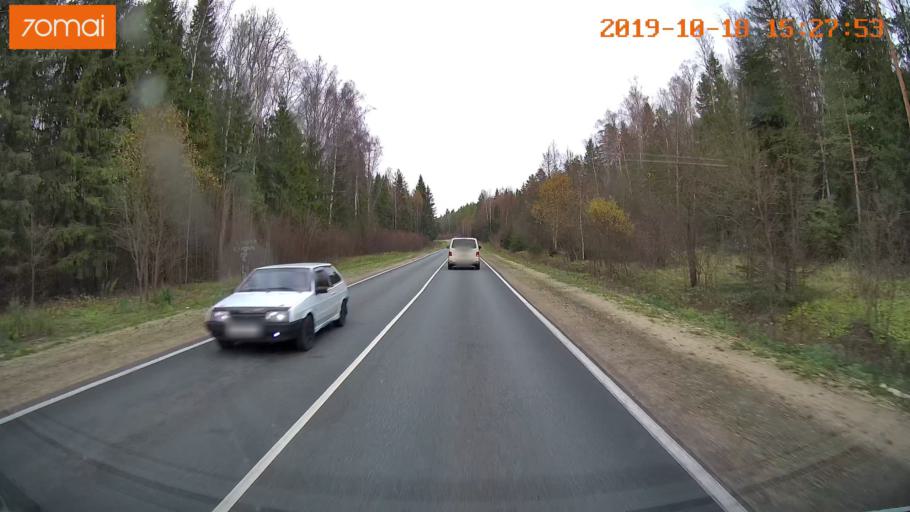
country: RU
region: Vladimir
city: Anopino
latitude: 55.7593
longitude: 40.6727
